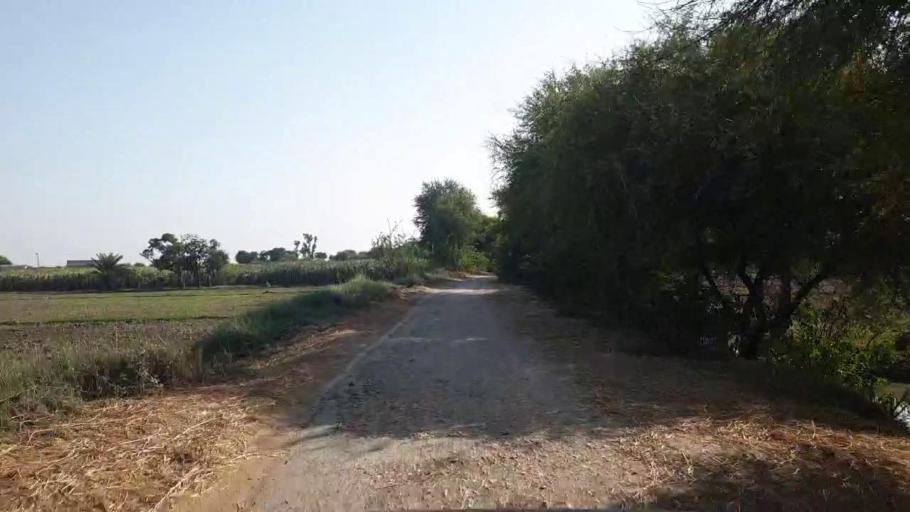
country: PK
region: Sindh
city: Matli
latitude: 25.0127
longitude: 68.7403
